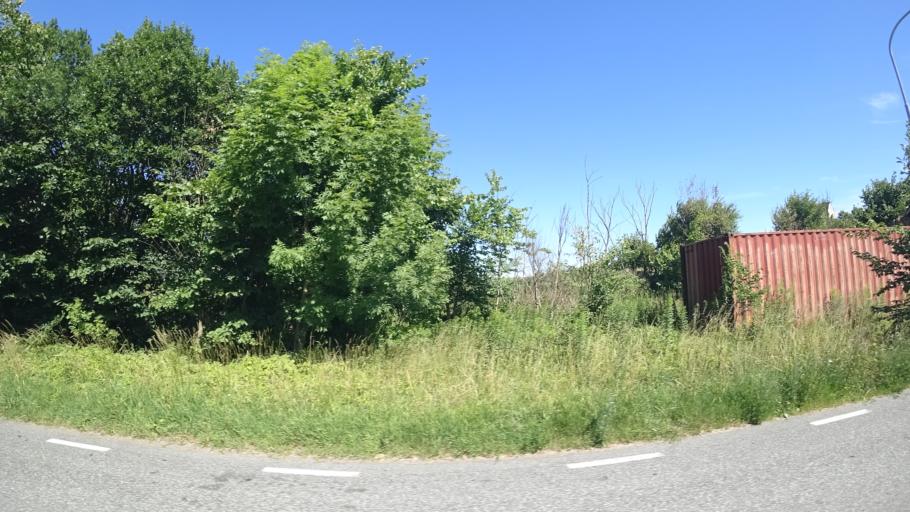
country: SE
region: Skane
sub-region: Kristianstads Kommun
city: Onnestad
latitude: 56.0732
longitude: 14.0805
